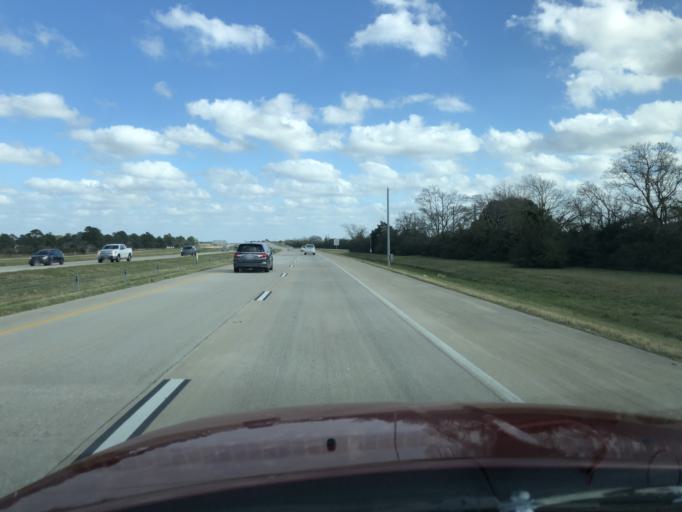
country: US
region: Texas
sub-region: Harris County
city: Cypress
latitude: 30.0501
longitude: -95.6879
